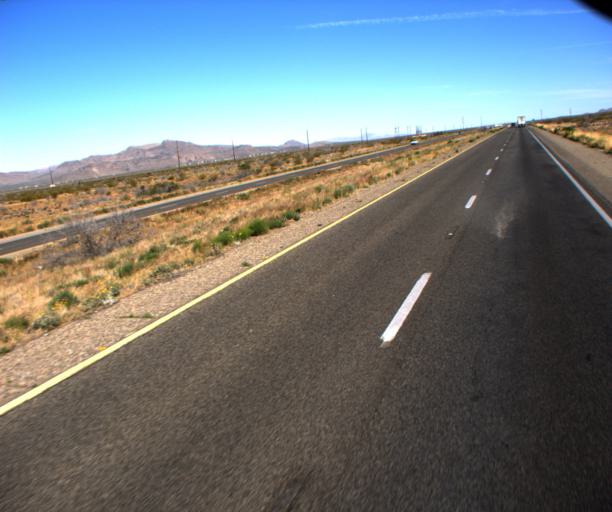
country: US
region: Arizona
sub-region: Mohave County
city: Golden Valley
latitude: 35.3133
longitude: -114.1986
